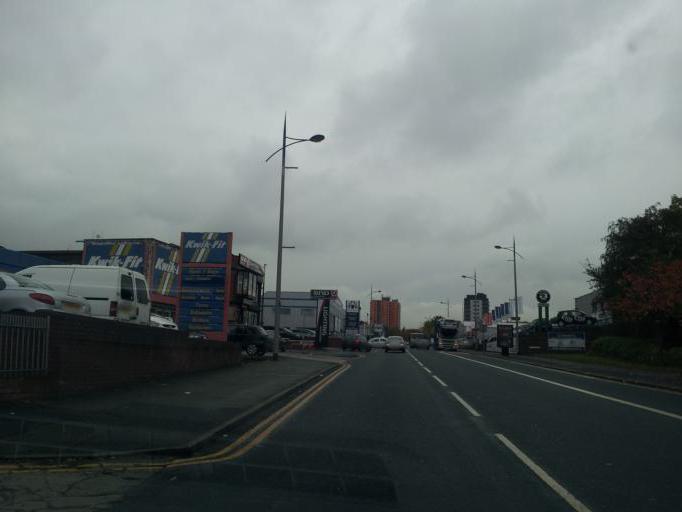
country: GB
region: England
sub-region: Manchester
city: Cheetham Hill
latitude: 53.4994
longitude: -2.2556
